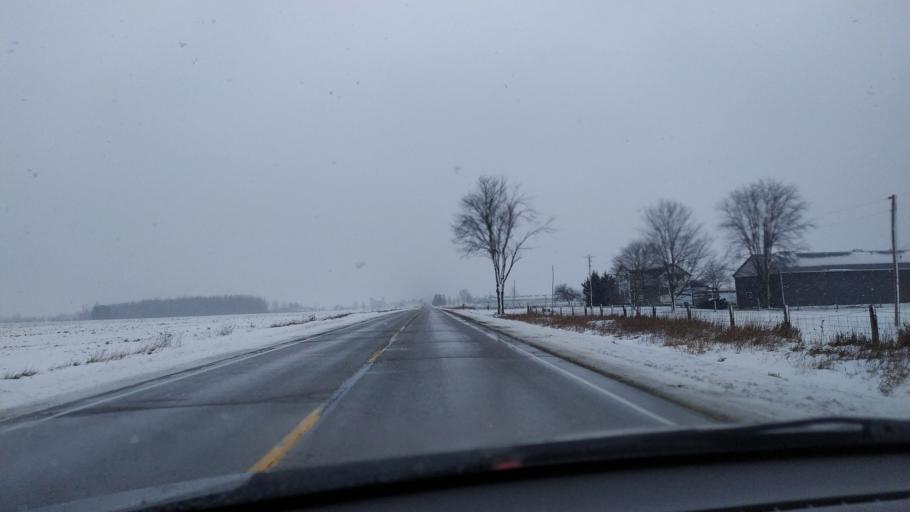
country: CA
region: Ontario
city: Stratford
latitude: 43.5131
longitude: -80.8848
